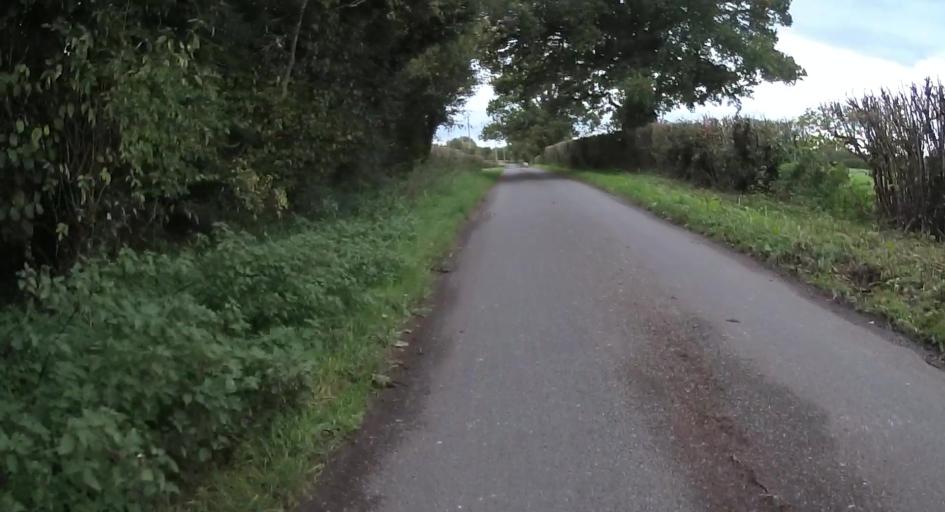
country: GB
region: England
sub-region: Hampshire
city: Four Marks
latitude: 51.1152
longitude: -1.0784
